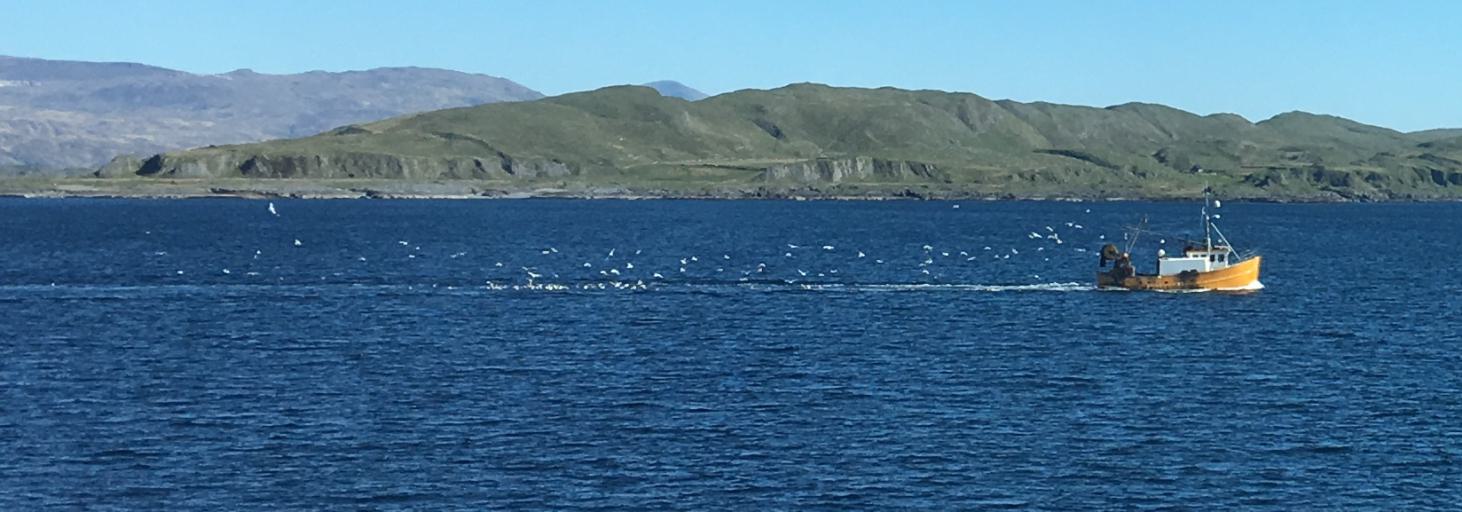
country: GB
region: Scotland
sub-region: Argyll and Bute
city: Oban
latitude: 56.4475
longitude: -5.6017
